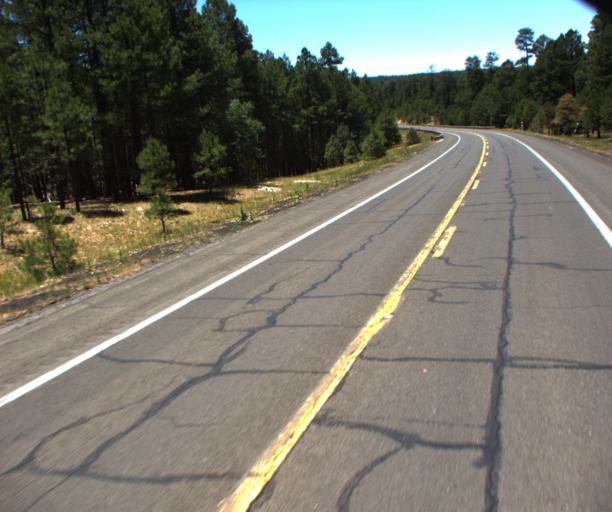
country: US
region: Arizona
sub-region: Gila County
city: Pine
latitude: 34.5523
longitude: -111.3079
